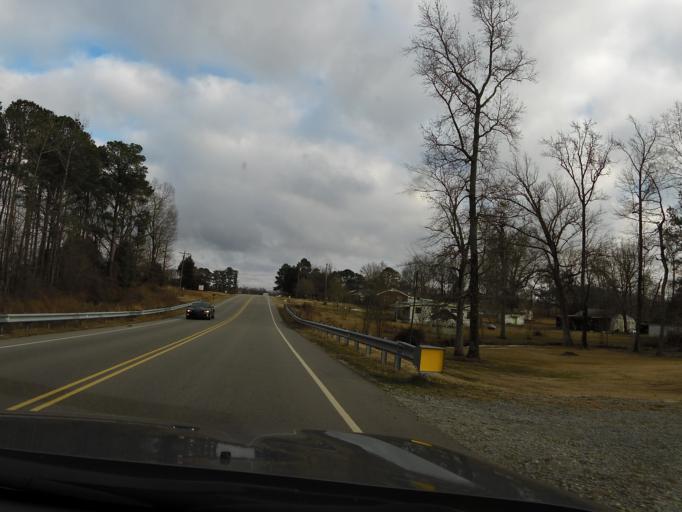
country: US
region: North Carolina
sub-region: Edgecombe County
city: Pinetops
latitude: 35.8121
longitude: -77.6556
